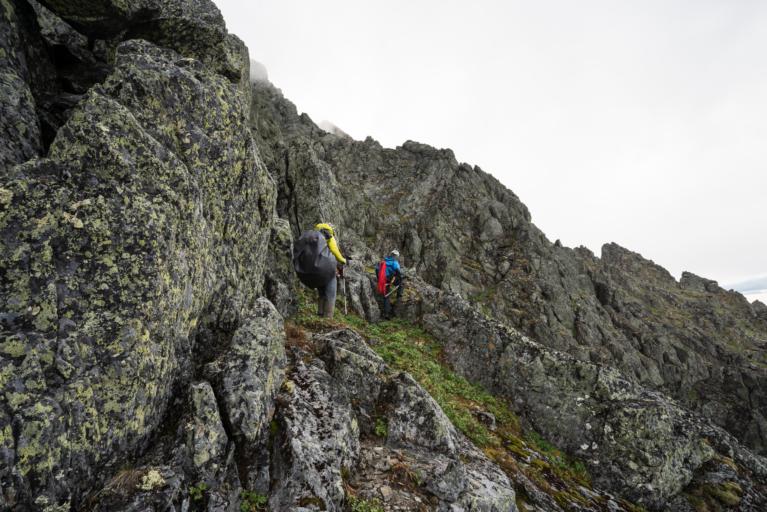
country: RU
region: Komi Republic
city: Synya
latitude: 64.7773
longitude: 58.8830
